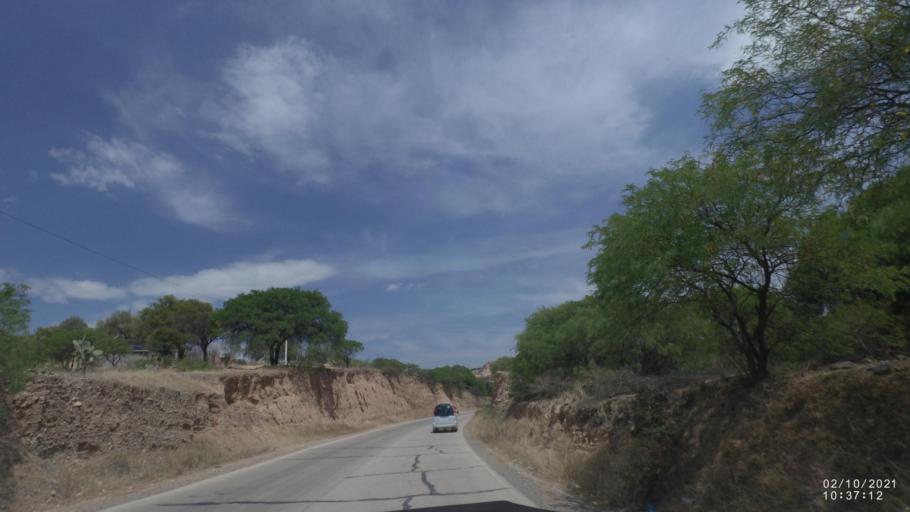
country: BO
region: Cochabamba
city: Capinota
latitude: -17.6452
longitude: -66.2625
